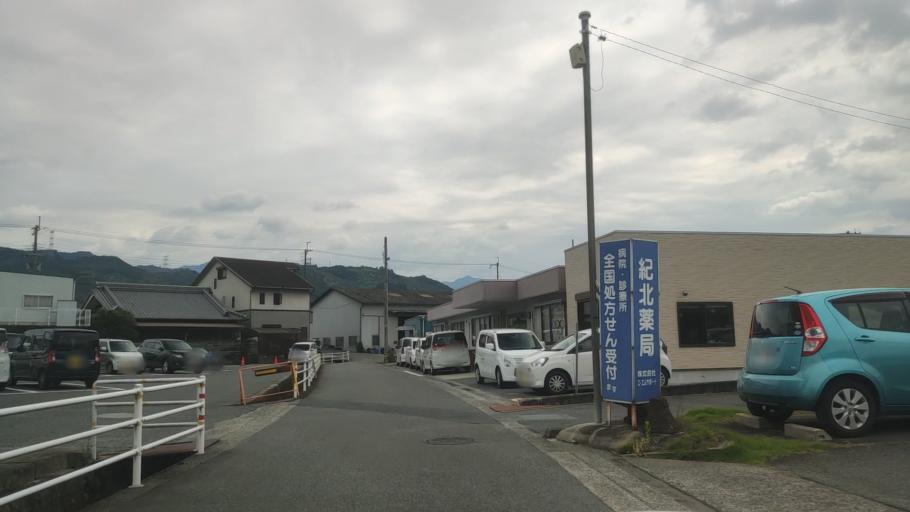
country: JP
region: Wakayama
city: Hashimoto
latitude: 34.3049
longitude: 135.5820
